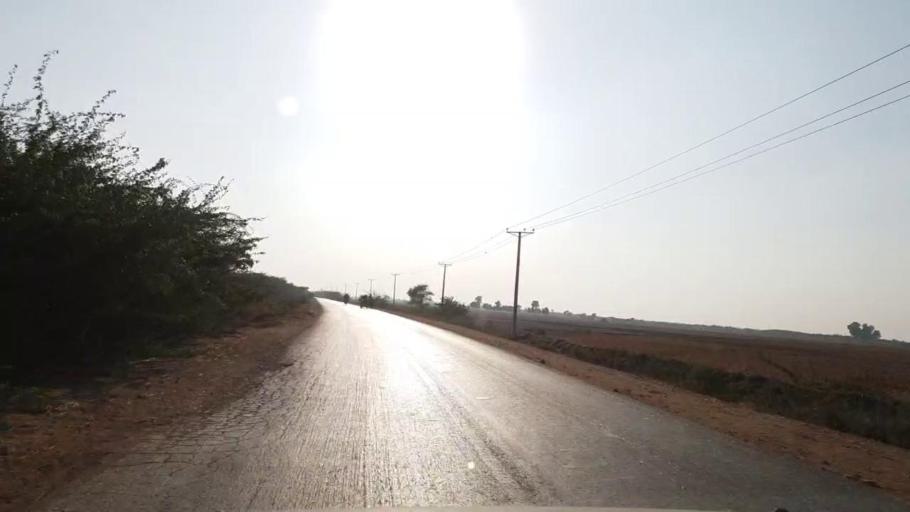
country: PK
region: Sindh
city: Bulri
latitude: 24.8024
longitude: 68.3091
